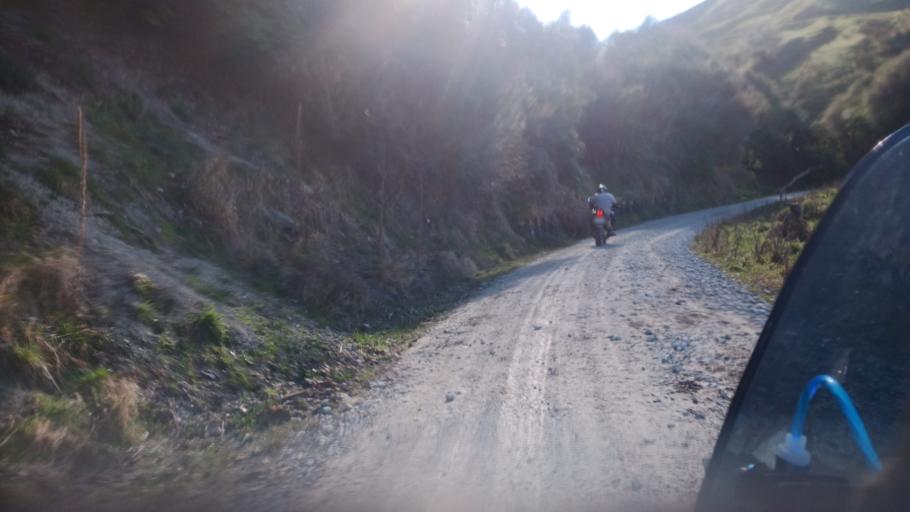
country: NZ
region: Hawke's Bay
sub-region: Wairoa District
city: Wairoa
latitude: -38.6673
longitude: 177.5358
